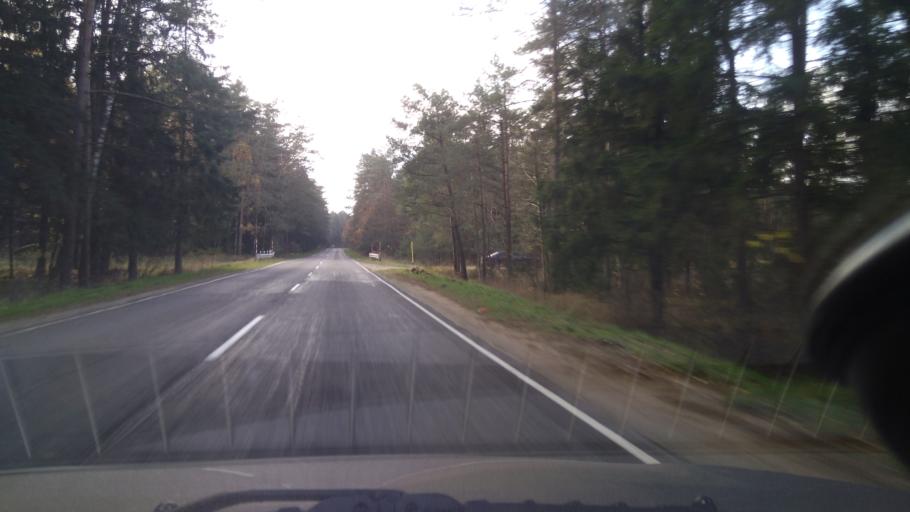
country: BY
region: Minsk
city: Slutsk
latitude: 53.2200
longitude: 27.5846
